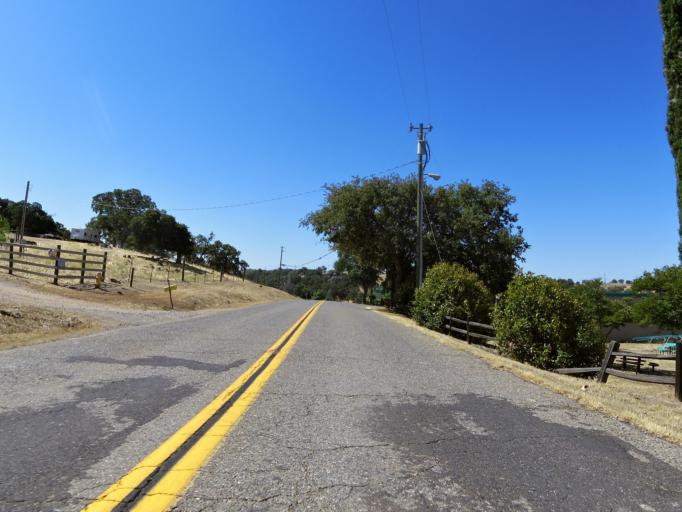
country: US
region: California
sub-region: Tuolumne County
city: Jamestown
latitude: 37.6814
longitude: -120.3229
